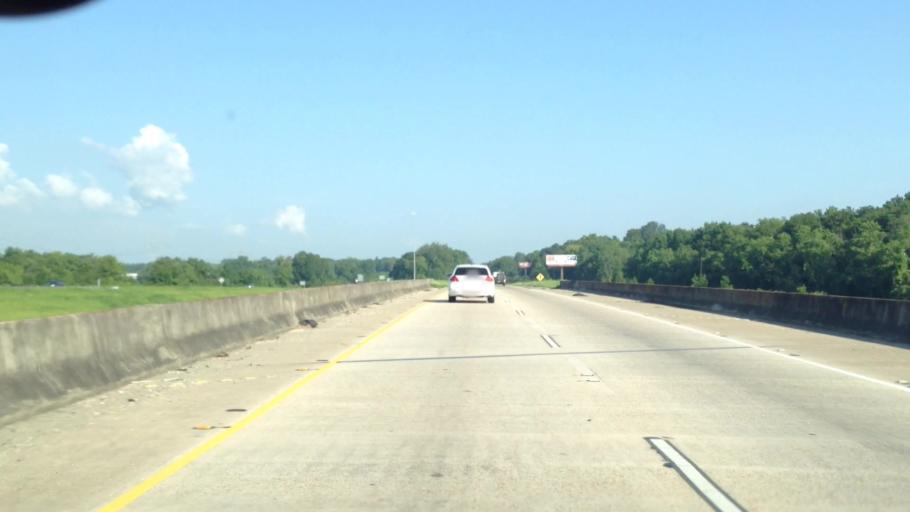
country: US
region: Louisiana
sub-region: Ascension Parish
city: Gonzales
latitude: 30.1925
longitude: -90.9198
